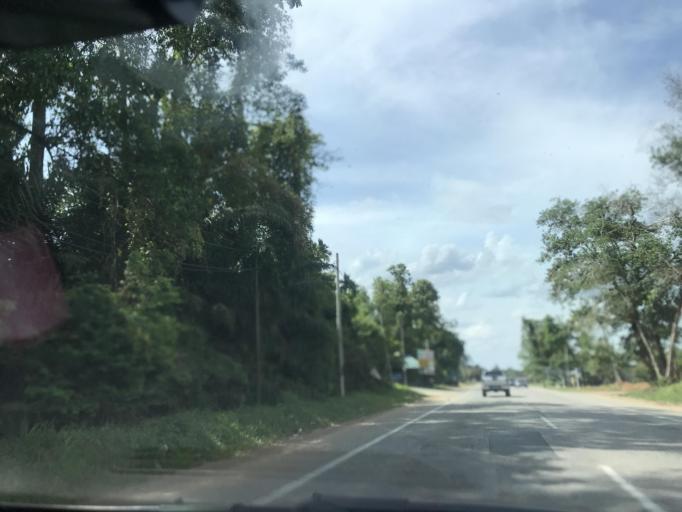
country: MY
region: Kelantan
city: Tanah Merah
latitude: 5.8405
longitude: 102.1596
